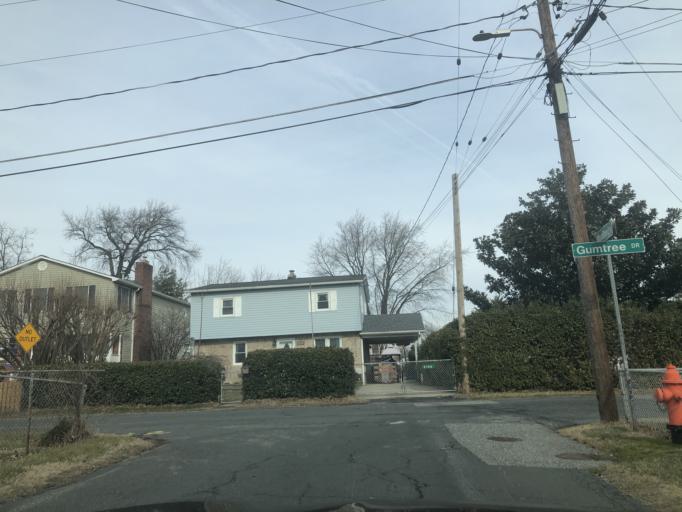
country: US
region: Maryland
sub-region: Baltimore County
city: Dundalk
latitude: 39.2657
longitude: -76.4835
